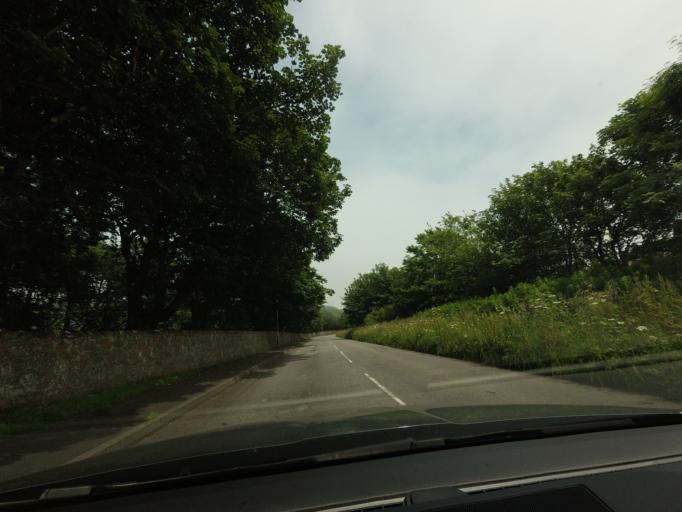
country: GB
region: Scotland
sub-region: Aberdeenshire
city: Peterhead
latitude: 57.4877
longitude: -1.7995
